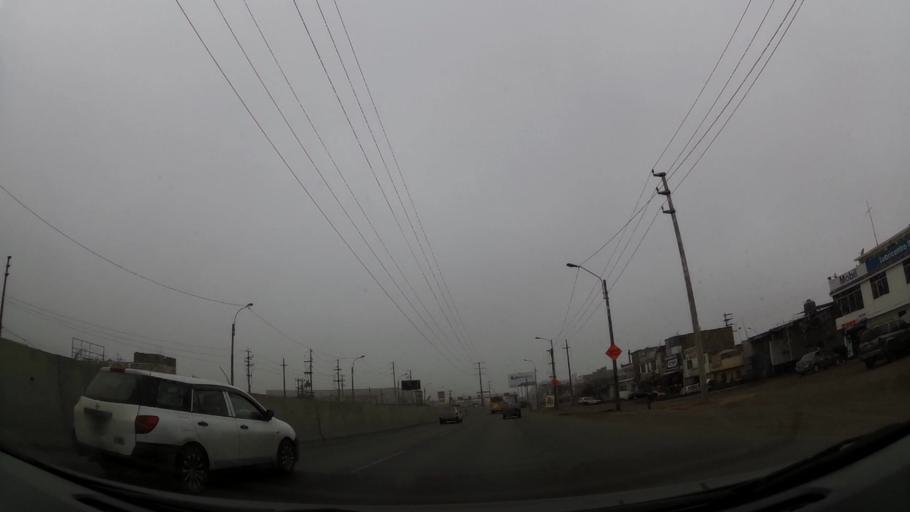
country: PE
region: Lima
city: Ventanilla
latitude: -11.8462
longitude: -77.0978
